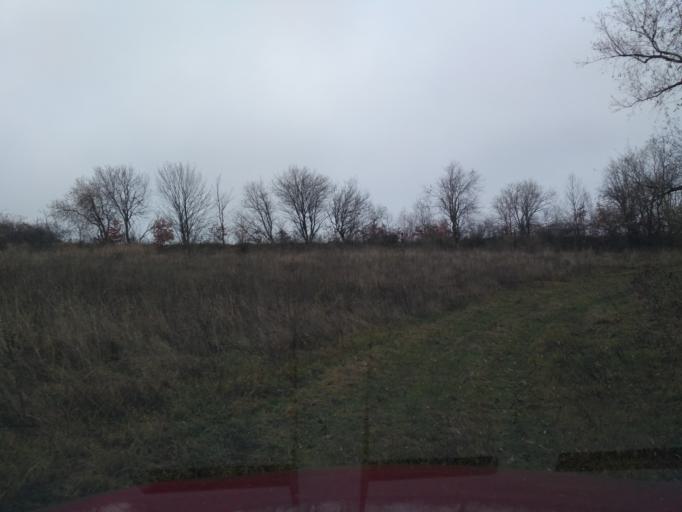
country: SK
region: Kosicky
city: Kosice
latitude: 48.7822
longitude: 21.2202
